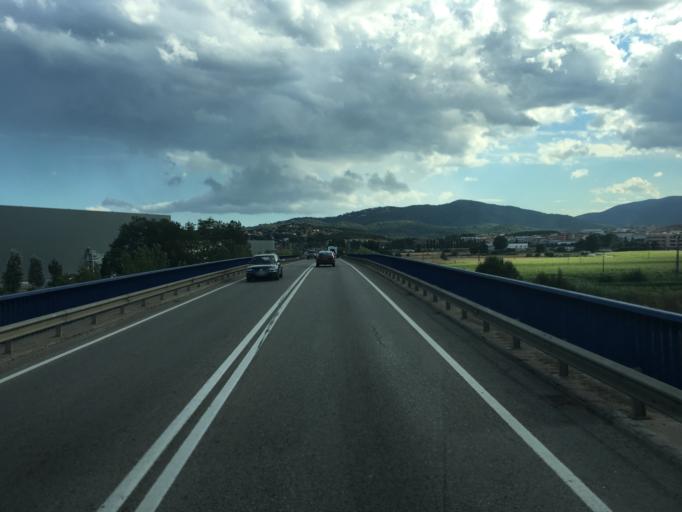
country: ES
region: Catalonia
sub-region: Provincia de Barcelona
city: Tordera
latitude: 41.7013
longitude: 2.7299
